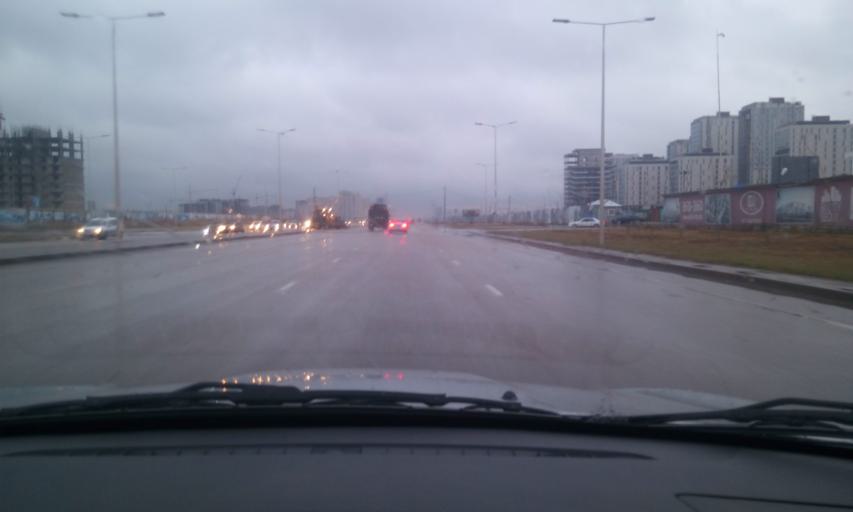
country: KZ
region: Astana Qalasy
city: Astana
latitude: 51.1281
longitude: 71.3974
